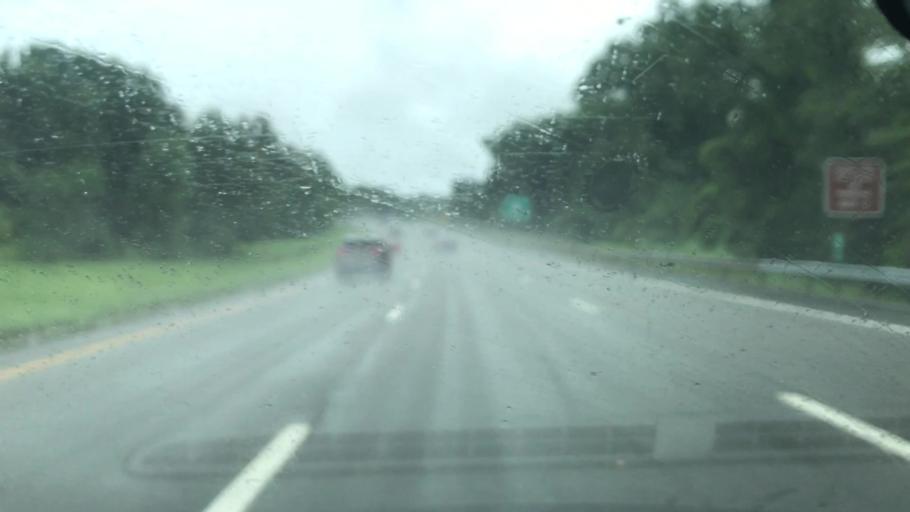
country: US
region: New York
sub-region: Westchester County
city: Briarcliff Manor
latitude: 41.2111
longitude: -73.8093
